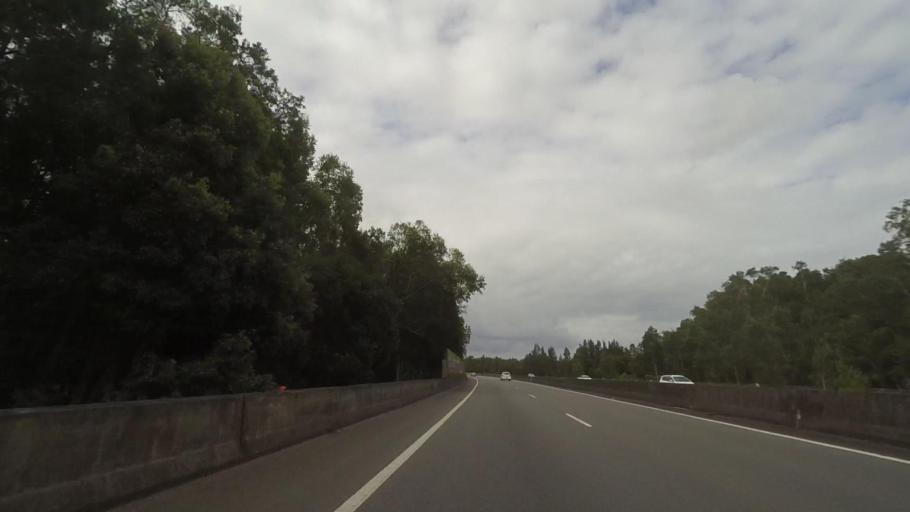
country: AU
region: New South Wales
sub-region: Port Stephens Shire
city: Raymond Terrace
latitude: -32.7704
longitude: 151.7610
